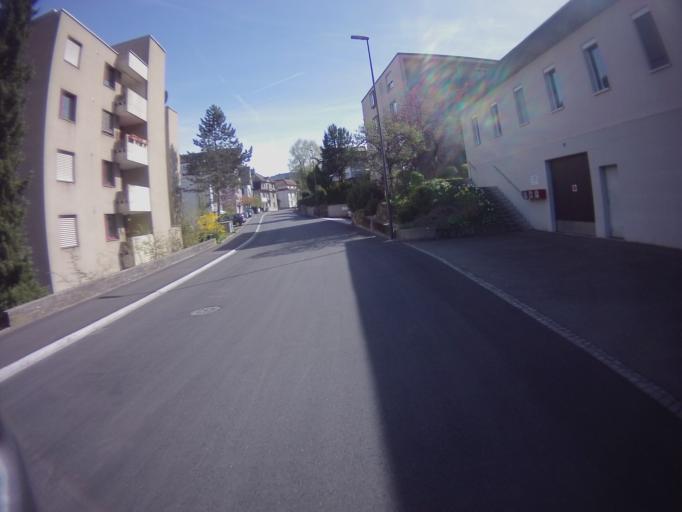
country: CH
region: Aargau
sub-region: Bezirk Baden
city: Baden
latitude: 47.4653
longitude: 8.3060
